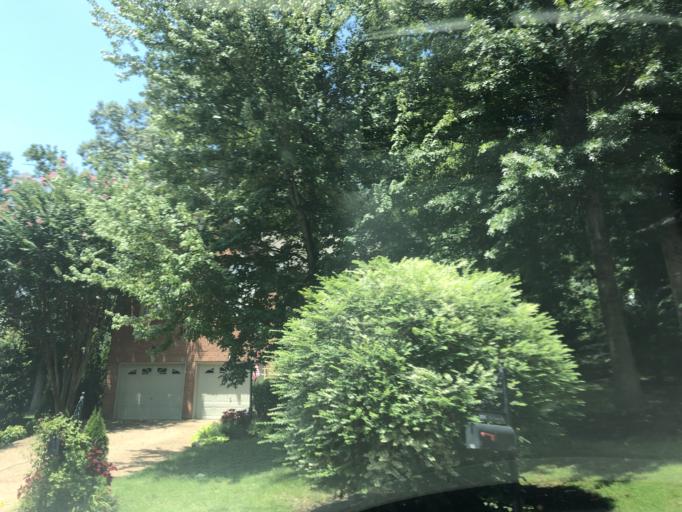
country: US
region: Tennessee
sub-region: Wilson County
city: Green Hill
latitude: 36.1910
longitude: -86.5878
